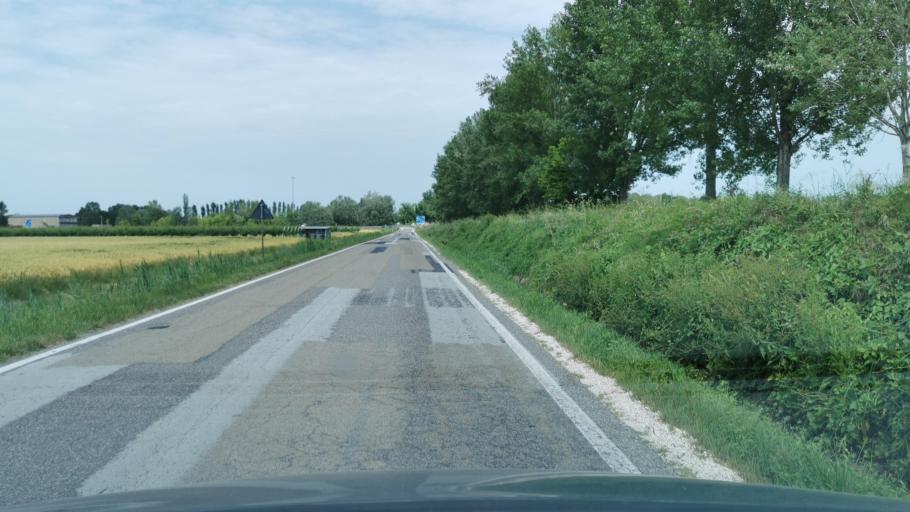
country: IT
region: Emilia-Romagna
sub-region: Provincia di Ravenna
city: Alfonsine
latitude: 44.4935
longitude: 12.0537
